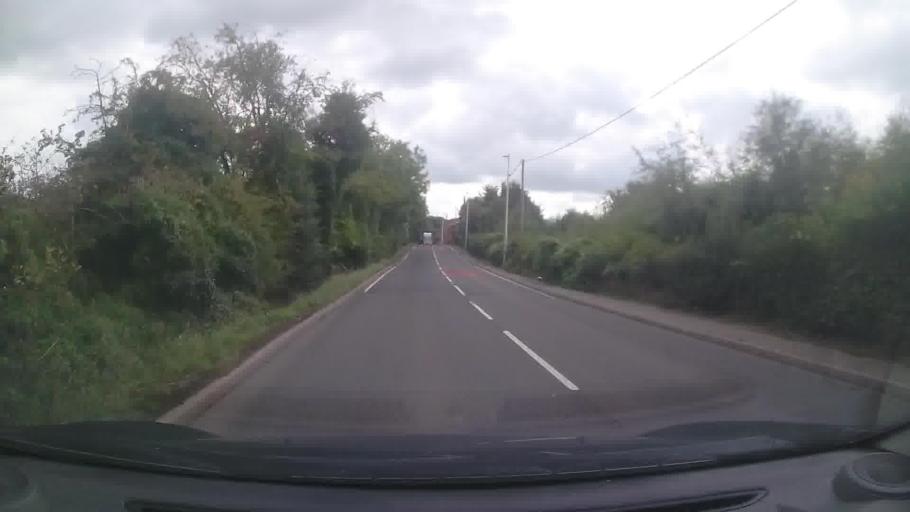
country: GB
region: England
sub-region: Shropshire
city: Pant
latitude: 52.7792
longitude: -3.0879
